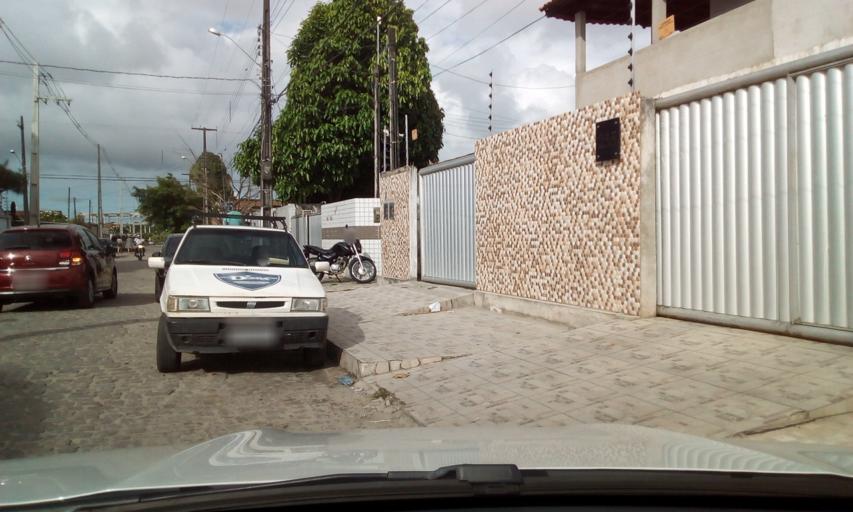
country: BR
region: Paraiba
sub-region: Joao Pessoa
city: Joao Pessoa
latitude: -7.1654
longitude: -34.8696
